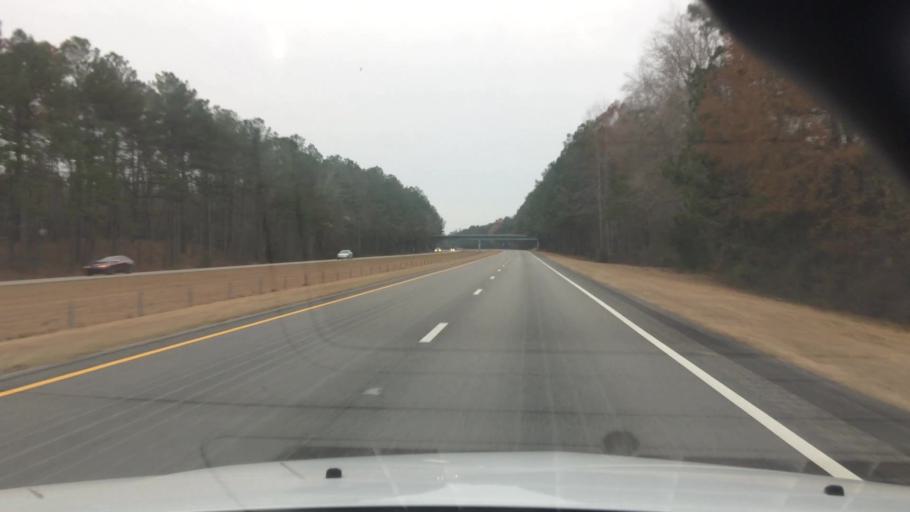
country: US
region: North Carolina
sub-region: Nash County
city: Spring Hope
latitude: 35.8873
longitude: -78.2069
